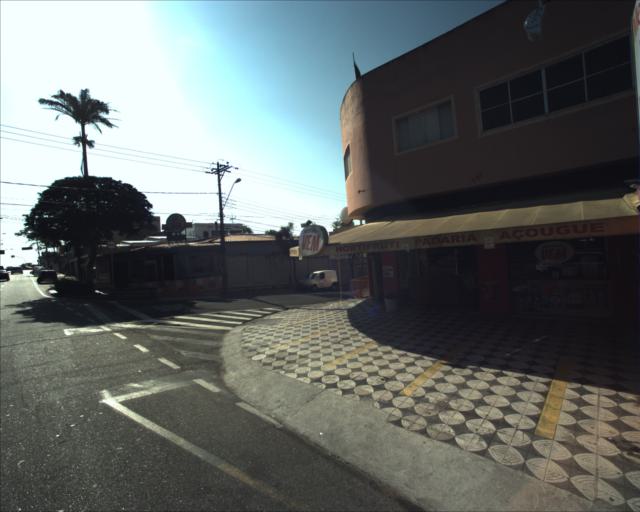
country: BR
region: Sao Paulo
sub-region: Sorocaba
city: Sorocaba
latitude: -23.4876
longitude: -47.4520
